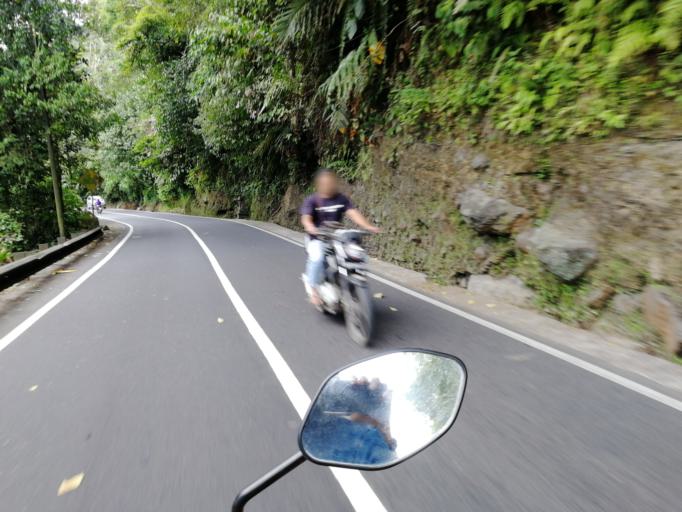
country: ID
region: Bali
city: Banjar Geriana Kangin
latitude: -8.4260
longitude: 115.4392
